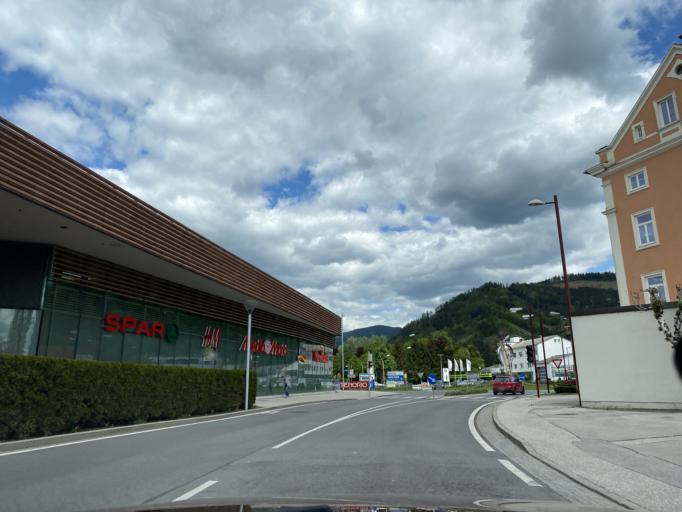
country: AT
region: Carinthia
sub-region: Politischer Bezirk Wolfsberg
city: Wolfsberg
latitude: 46.8422
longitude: 14.8409
